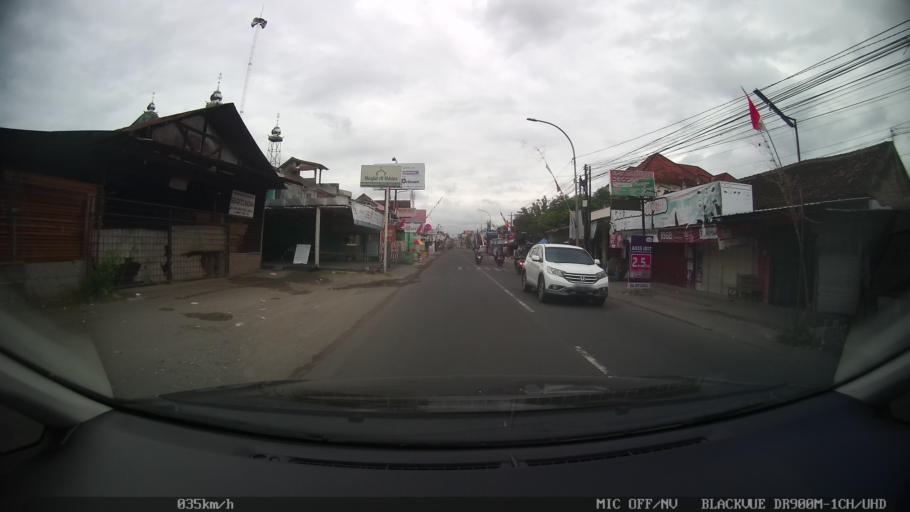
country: ID
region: Daerah Istimewa Yogyakarta
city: Sewon
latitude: -7.8462
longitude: 110.3910
